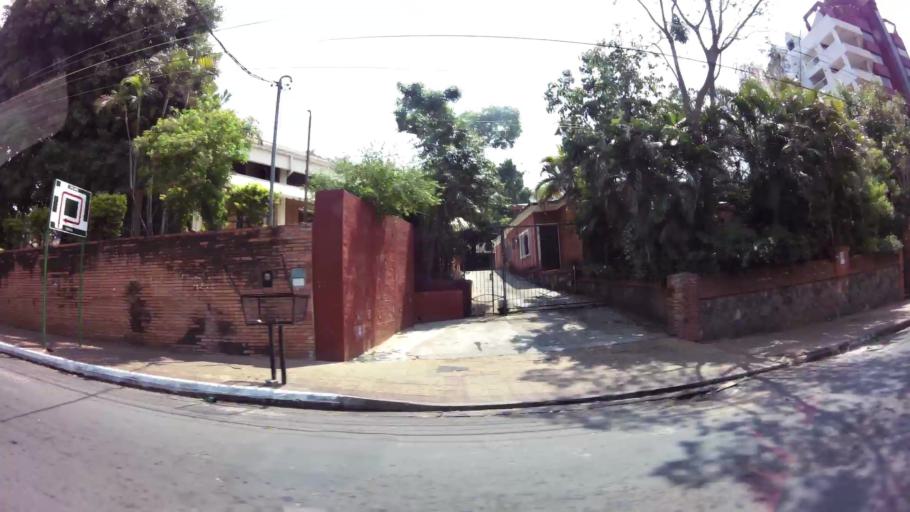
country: PY
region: Asuncion
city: Asuncion
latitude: -25.2871
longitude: -57.6096
